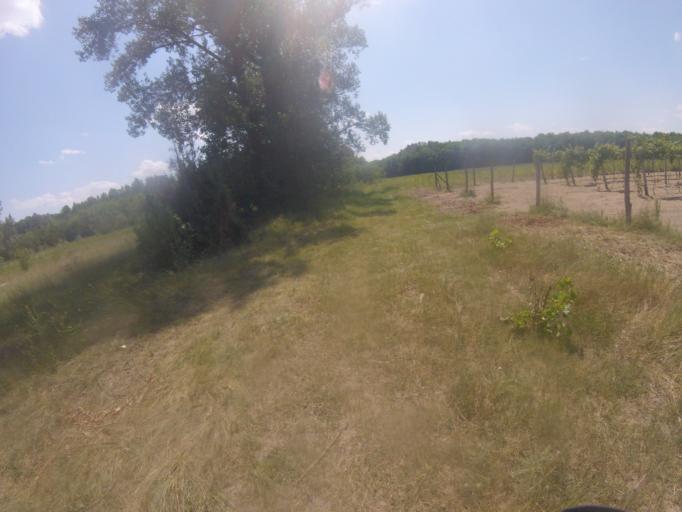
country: HU
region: Bacs-Kiskun
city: Jaszszentlaszlo
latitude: 46.6039
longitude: 19.7116
